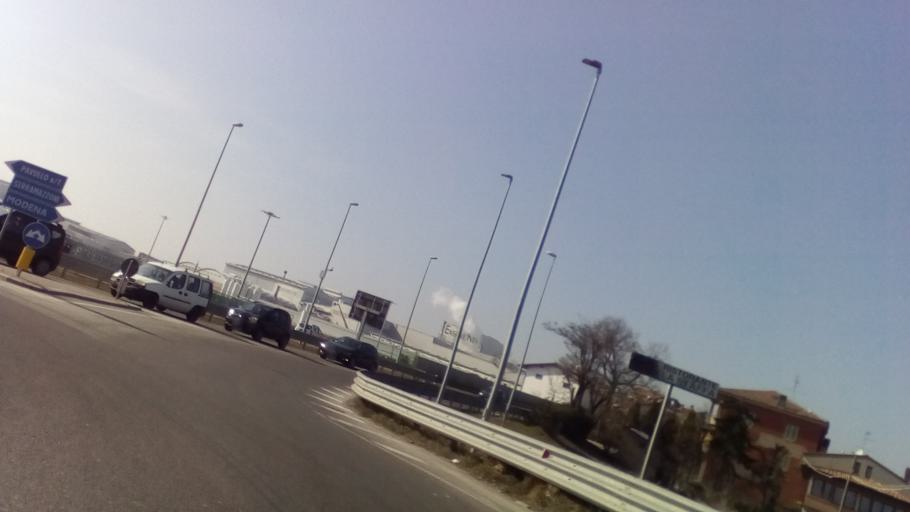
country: IT
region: Emilia-Romagna
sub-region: Provincia di Modena
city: Sant'Antonio
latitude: 44.3752
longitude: 10.8290
